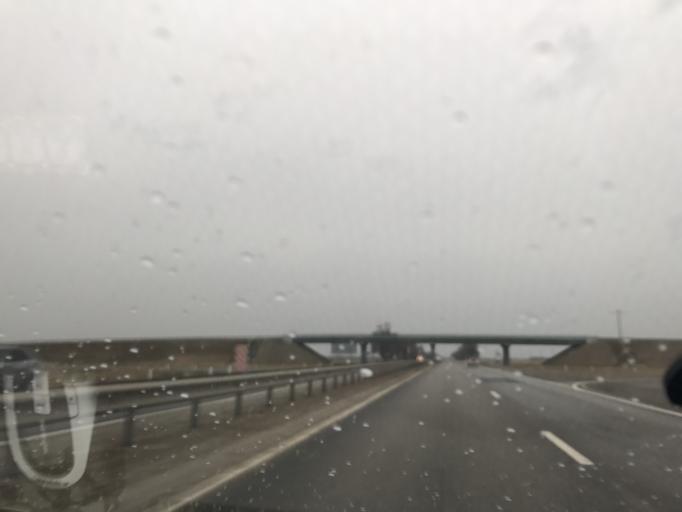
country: RU
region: Krasnodarskiy
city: Pavlovskaya
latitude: 46.1613
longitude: 39.8439
